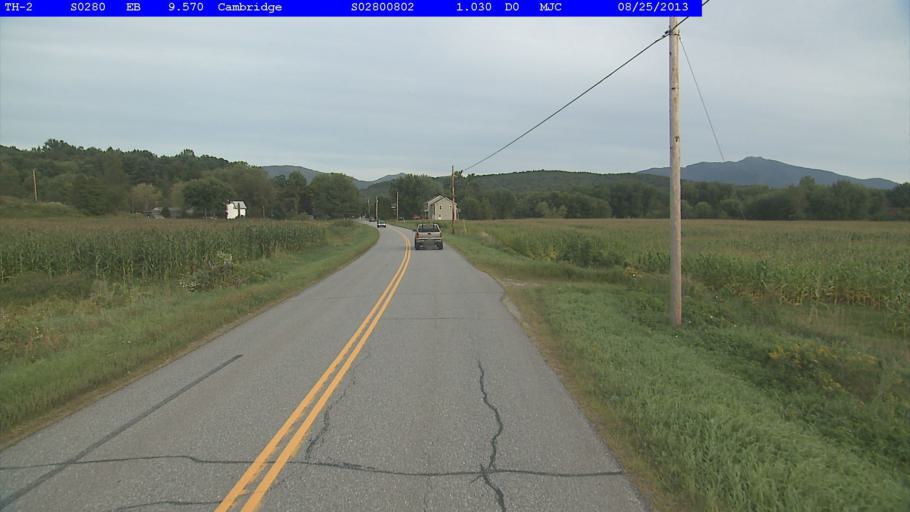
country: US
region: Vermont
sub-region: Chittenden County
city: Jericho
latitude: 44.6499
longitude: -72.8762
